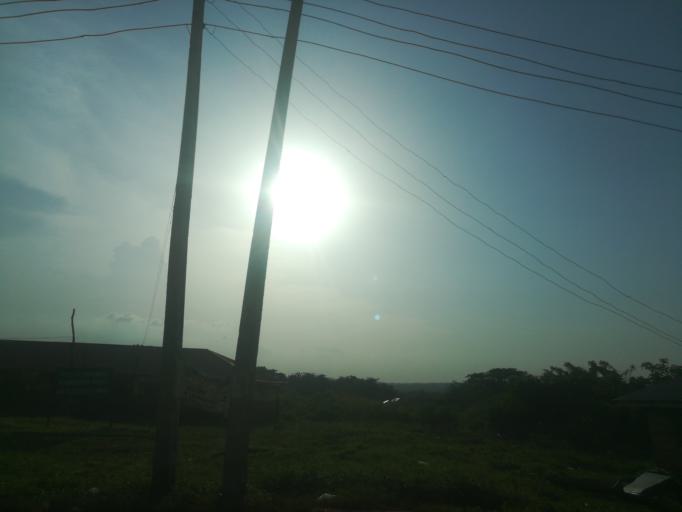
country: NG
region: Oyo
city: Moniya
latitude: 7.5620
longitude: 3.8865
